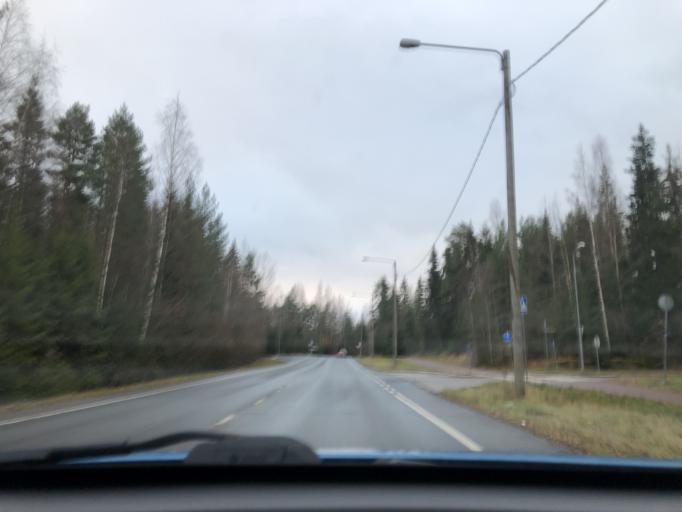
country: FI
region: Pirkanmaa
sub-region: Tampere
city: Kangasala
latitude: 61.5278
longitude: 23.9537
